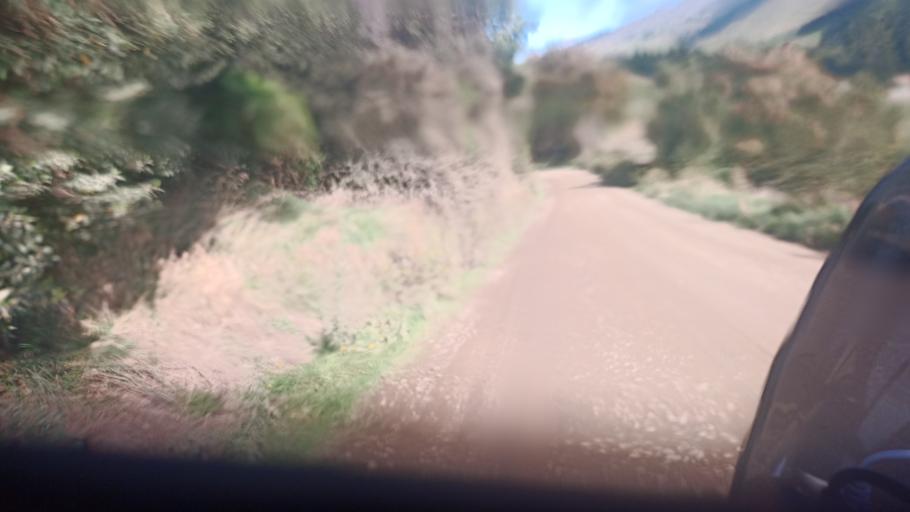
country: NZ
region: Bay of Plenty
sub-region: Opotiki District
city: Opotiki
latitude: -38.4371
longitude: 177.5443
